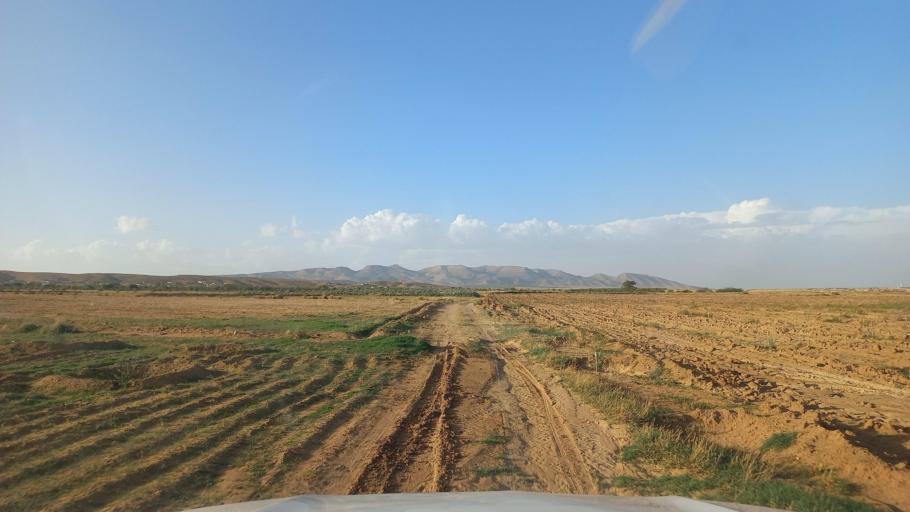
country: TN
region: Al Qasrayn
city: Sbiba
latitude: 35.3619
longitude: 9.0210
